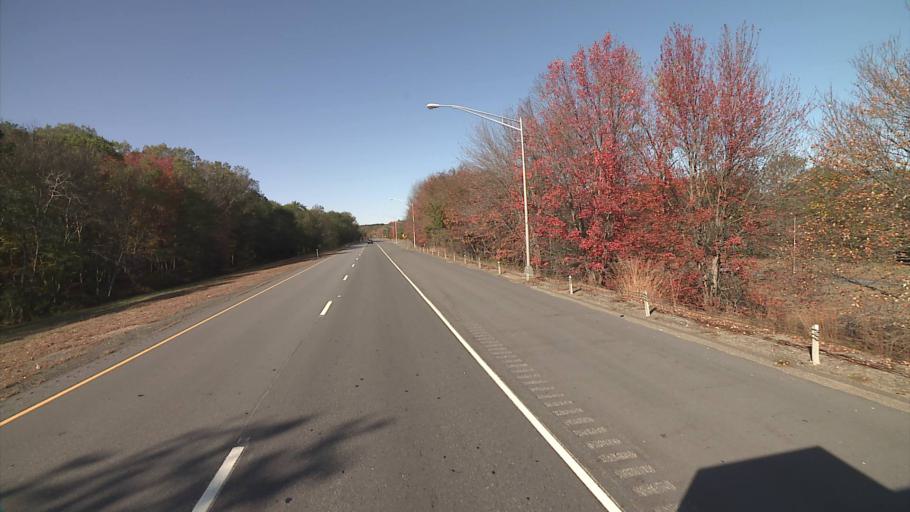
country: US
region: Connecticut
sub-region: Windham County
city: Willimantic
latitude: 41.7307
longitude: -72.2164
